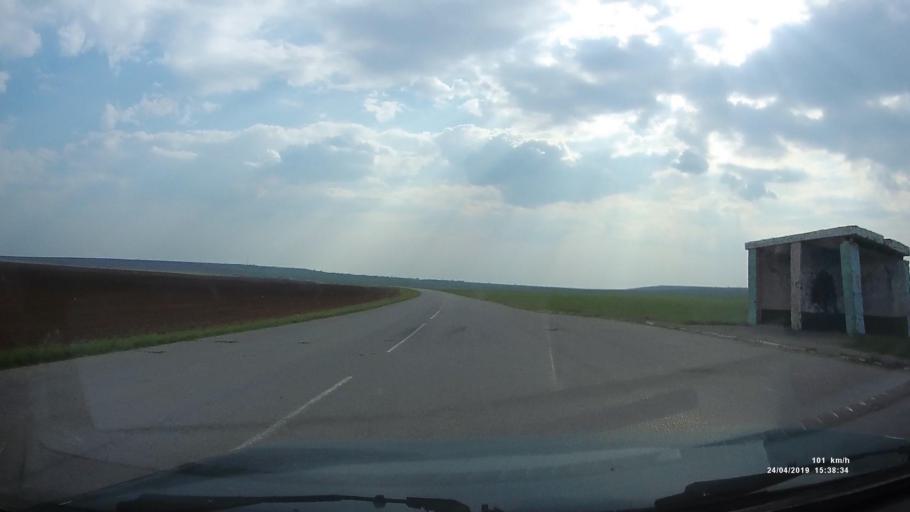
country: RU
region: Kalmykiya
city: Yashalta
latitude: 46.5966
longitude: 42.8258
